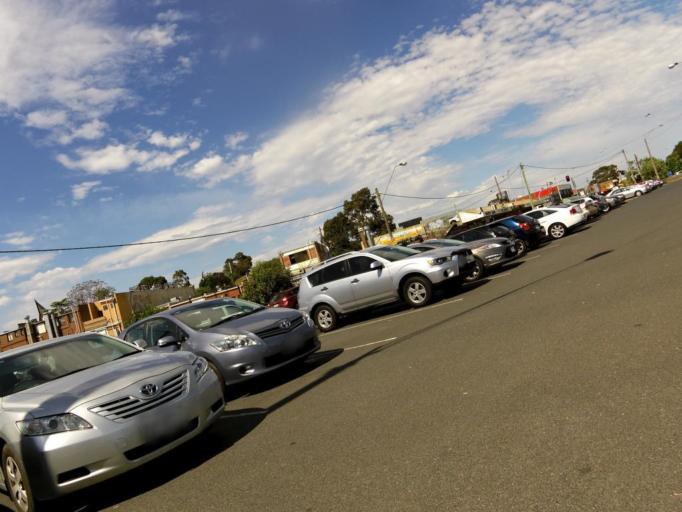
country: AU
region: Victoria
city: Clayton
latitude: -37.9233
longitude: 145.1189
